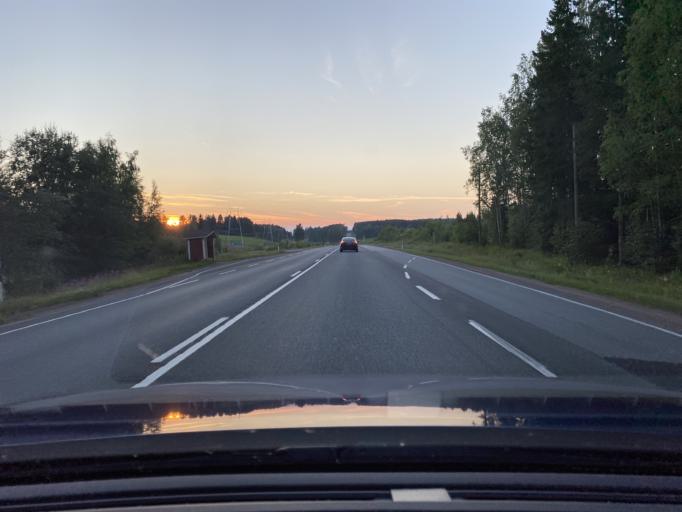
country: FI
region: Pirkanmaa
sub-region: Luoteis-Pirkanmaa
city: Ikaalinen
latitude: 61.8093
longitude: 22.9619
